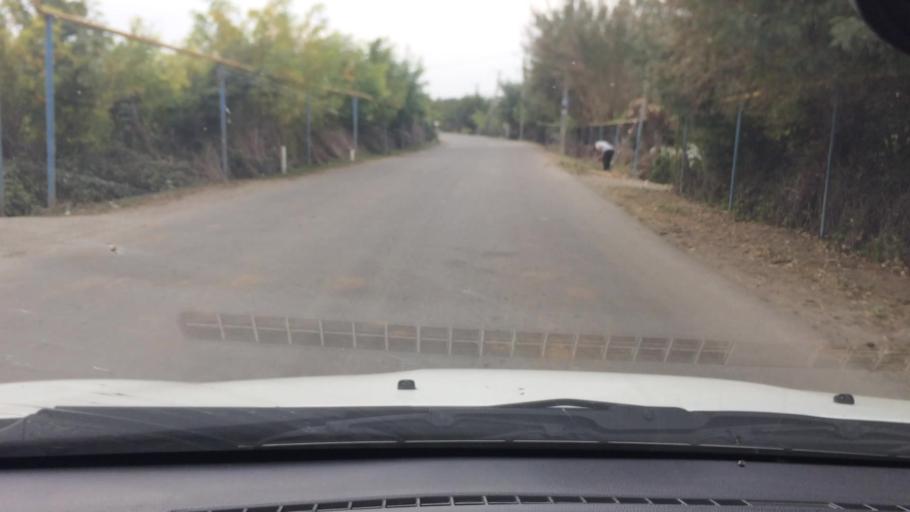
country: AM
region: Tavush
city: Berdavan
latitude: 41.3524
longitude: 44.9680
